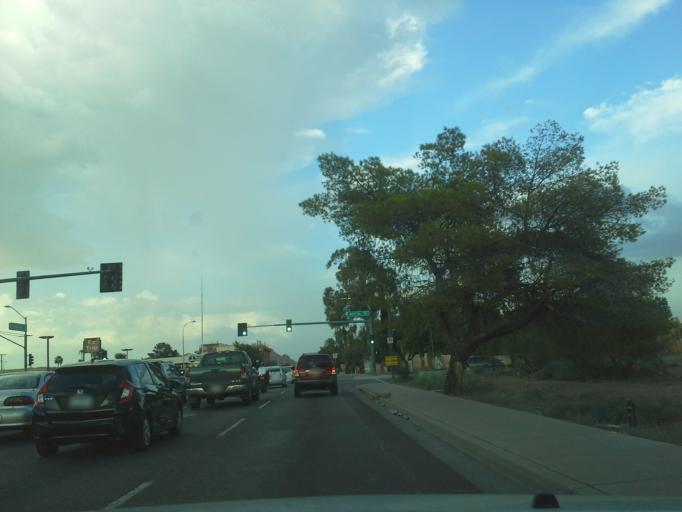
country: US
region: Arizona
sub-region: Maricopa County
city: Tempe Junction
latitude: 33.4656
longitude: -111.9962
